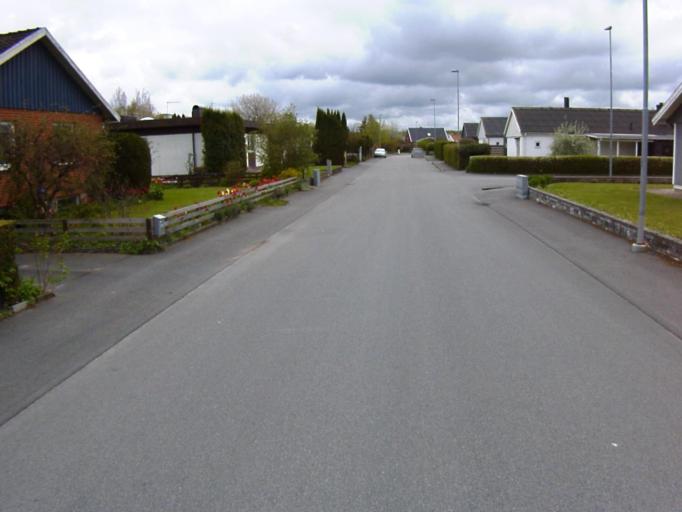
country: SE
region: Skane
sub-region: Kristianstads Kommun
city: Kristianstad
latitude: 56.0529
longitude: 14.1759
